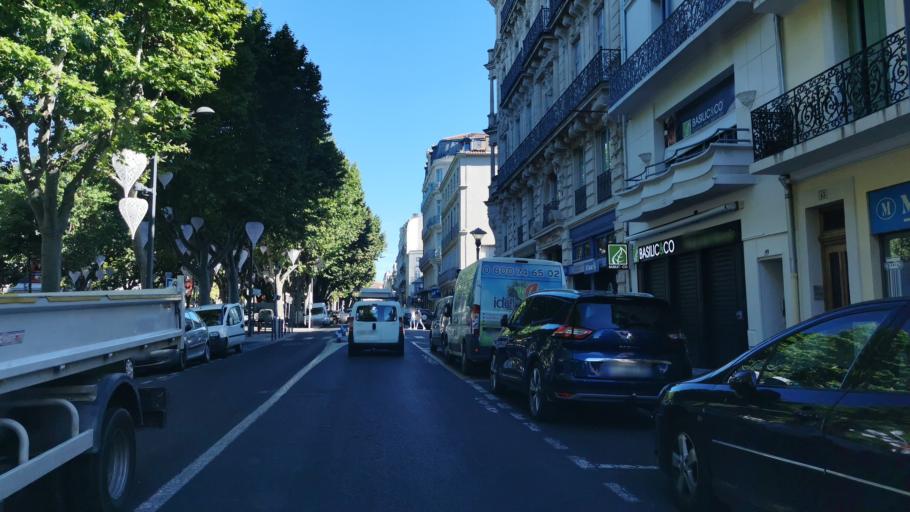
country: FR
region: Languedoc-Roussillon
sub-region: Departement de l'Herault
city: Beziers
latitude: 43.3413
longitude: 3.2182
